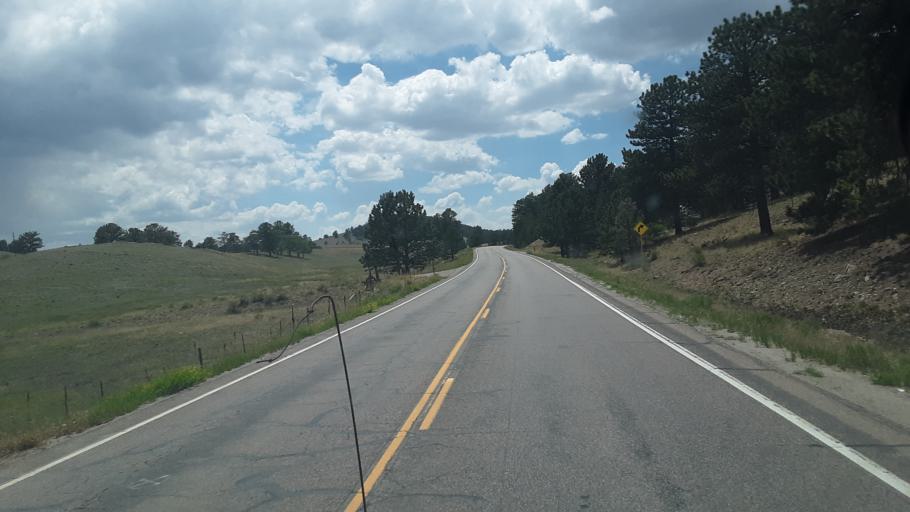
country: US
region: Colorado
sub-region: Custer County
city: Westcliffe
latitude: 38.1607
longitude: -105.2542
